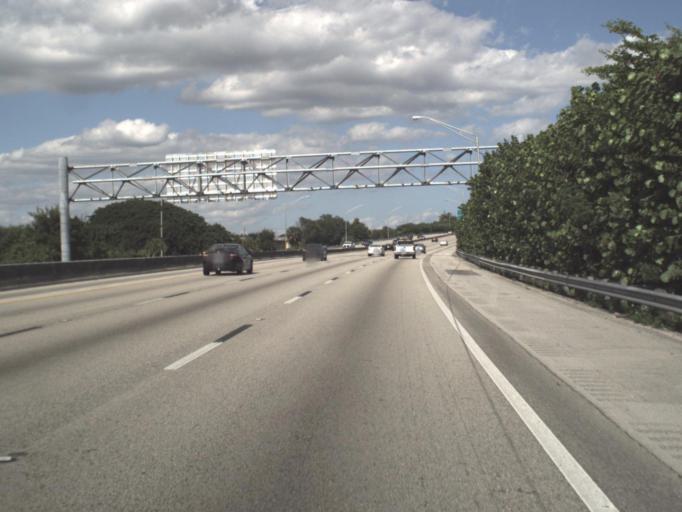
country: US
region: Florida
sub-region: Broward County
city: Miramar
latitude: 25.9903
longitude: -80.2277
